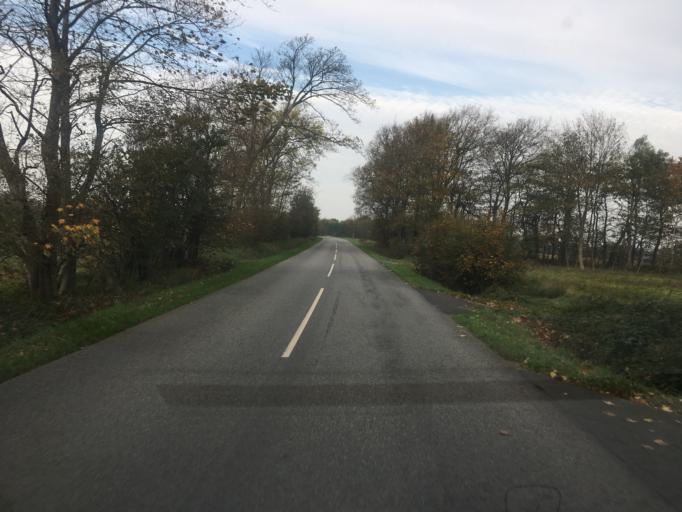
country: DK
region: South Denmark
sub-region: Tonder Kommune
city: Toftlund
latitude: 55.1114
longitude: 9.0866
